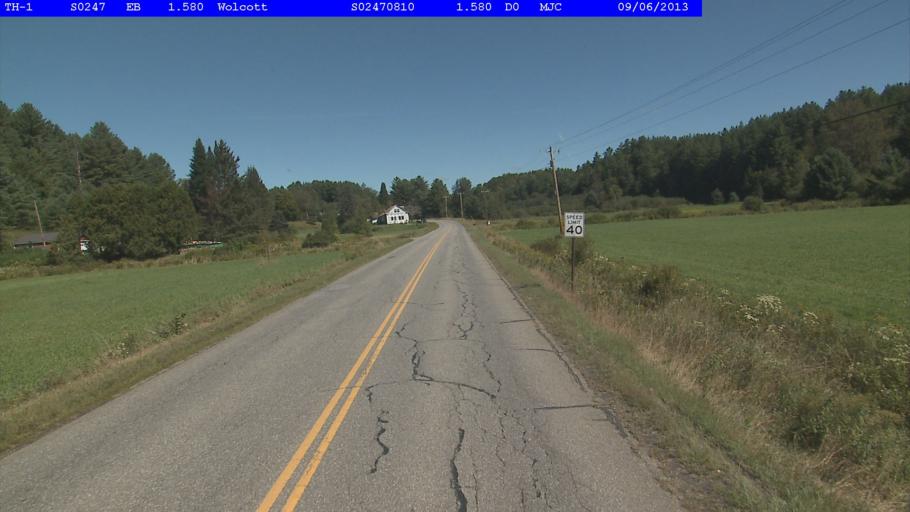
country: US
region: Vermont
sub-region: Lamoille County
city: Morrisville
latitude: 44.5786
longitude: -72.4764
